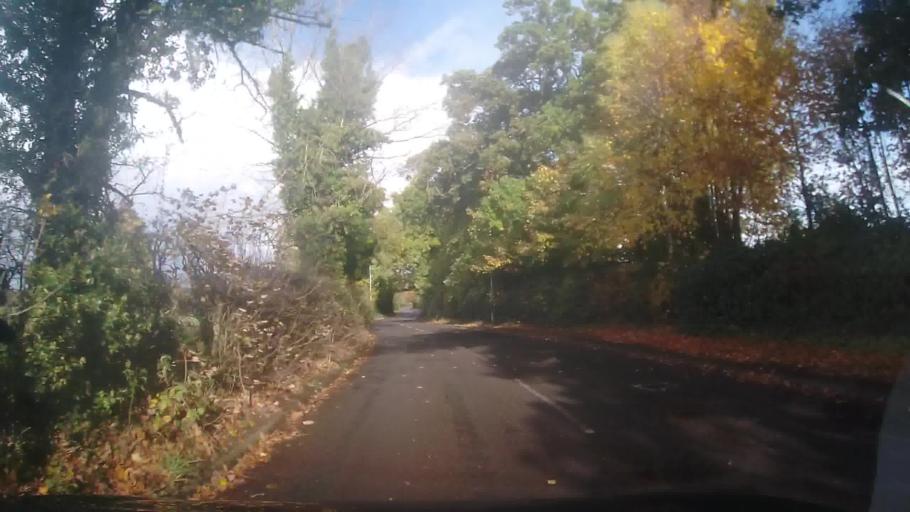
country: GB
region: England
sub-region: Shropshire
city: Whitchurch
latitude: 52.9579
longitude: -2.6797
